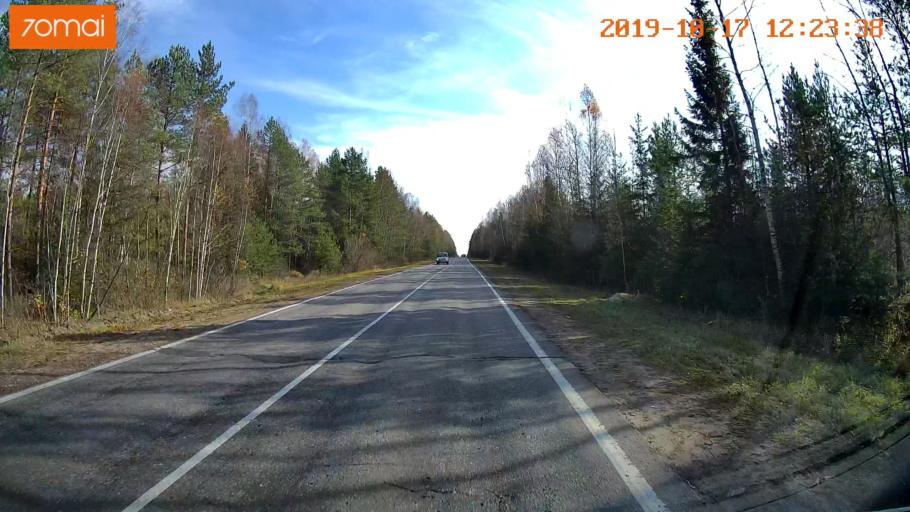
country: RU
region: Rjazan
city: Gus'-Zheleznyy
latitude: 55.0424
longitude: 41.1976
